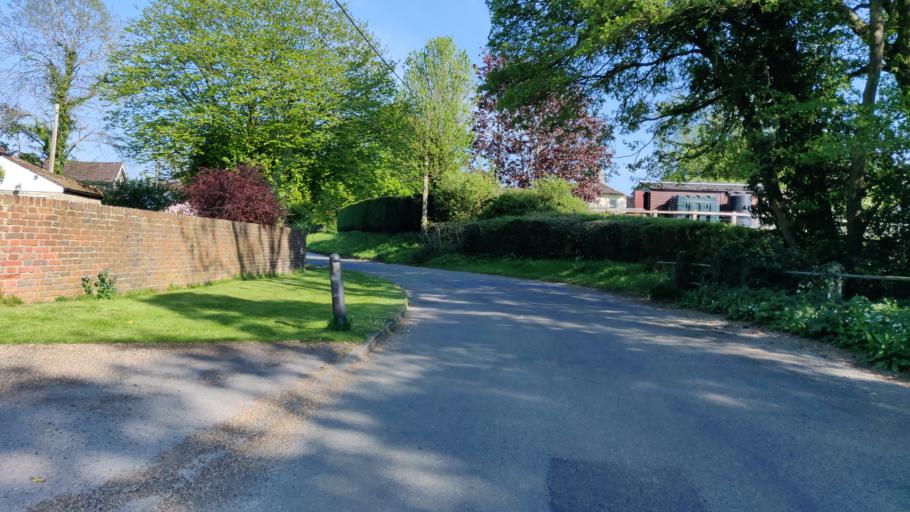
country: GB
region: England
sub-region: West Sussex
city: Southwater
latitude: 51.0296
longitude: -0.3883
